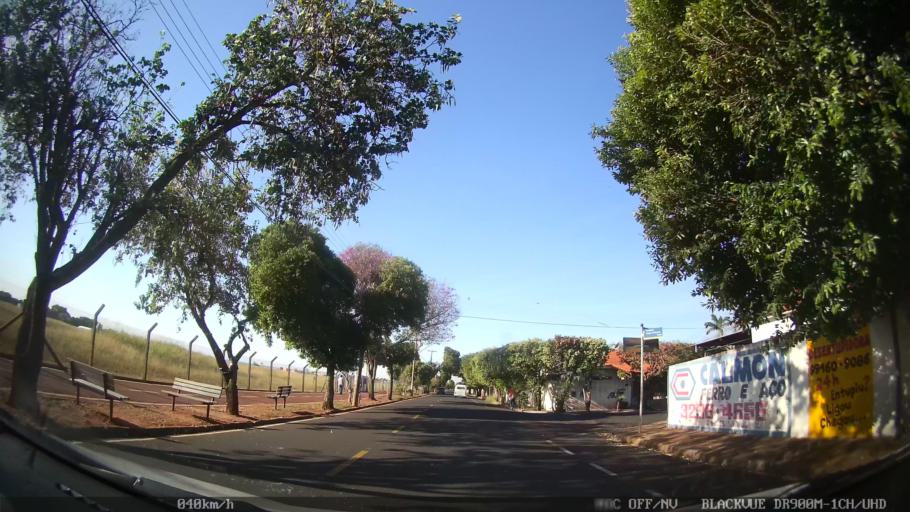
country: BR
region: Sao Paulo
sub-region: Sao Jose Do Rio Preto
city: Sao Jose do Rio Preto
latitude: -20.8178
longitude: -49.4055
